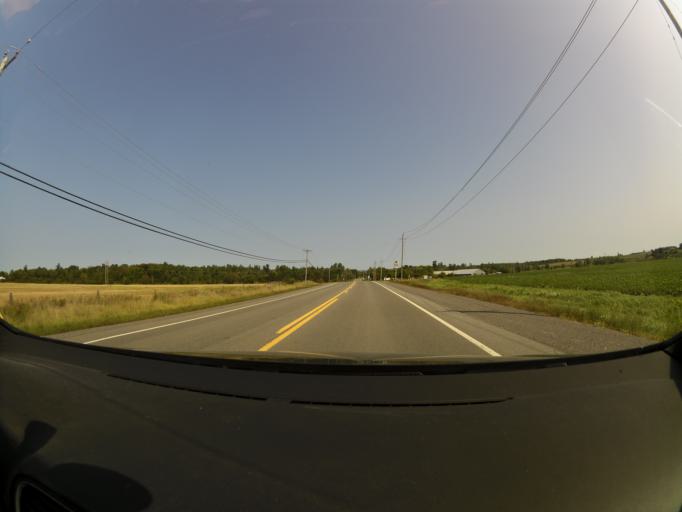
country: CA
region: Ontario
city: Arnprior
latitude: 45.4201
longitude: -76.2626
